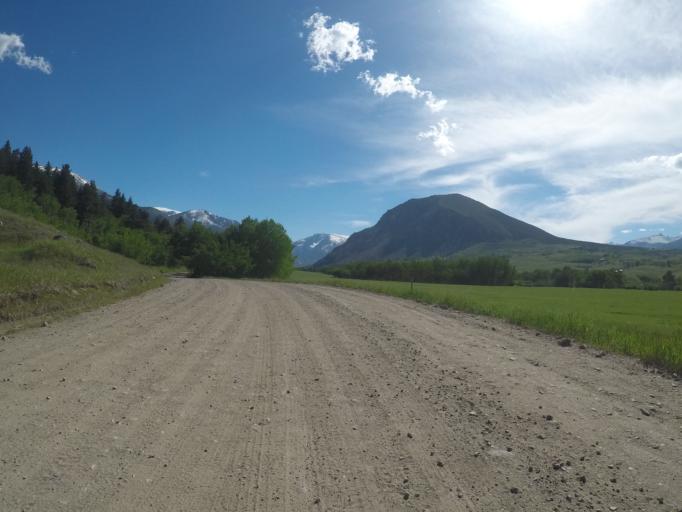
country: US
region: Montana
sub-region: Stillwater County
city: Absarokee
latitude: 45.2849
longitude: -109.5435
